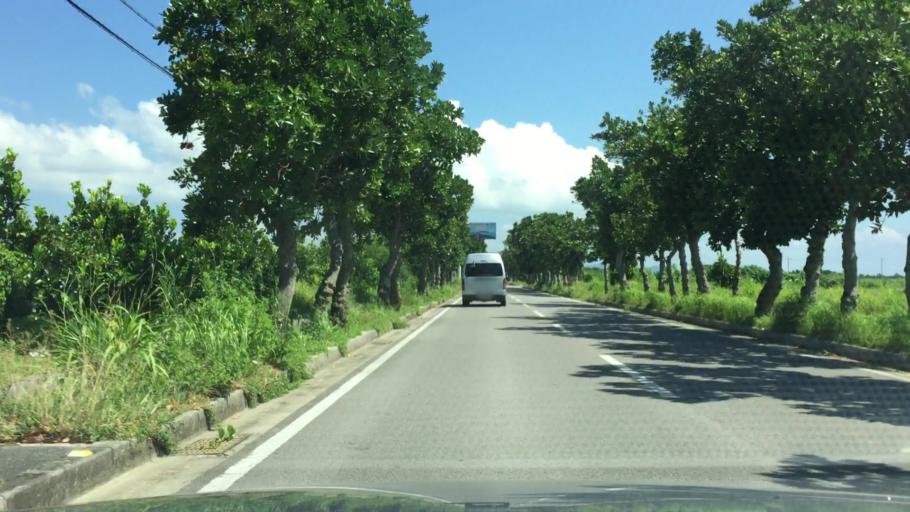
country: JP
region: Okinawa
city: Ishigaki
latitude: 24.3729
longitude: 124.2462
